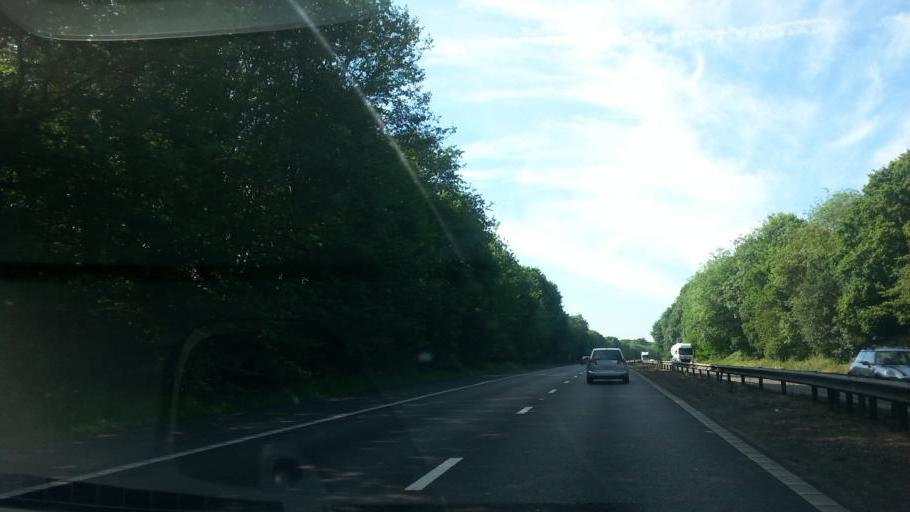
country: GB
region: England
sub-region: Hertfordshire
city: Knebworth
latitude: 51.8574
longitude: -0.1960
